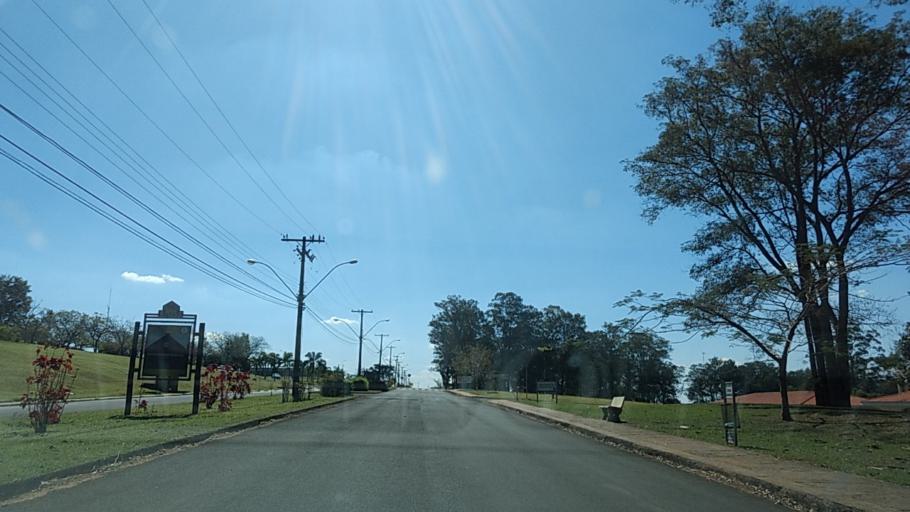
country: BR
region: Sao Paulo
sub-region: Botucatu
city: Botucatu
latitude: -22.8534
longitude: -48.4326
